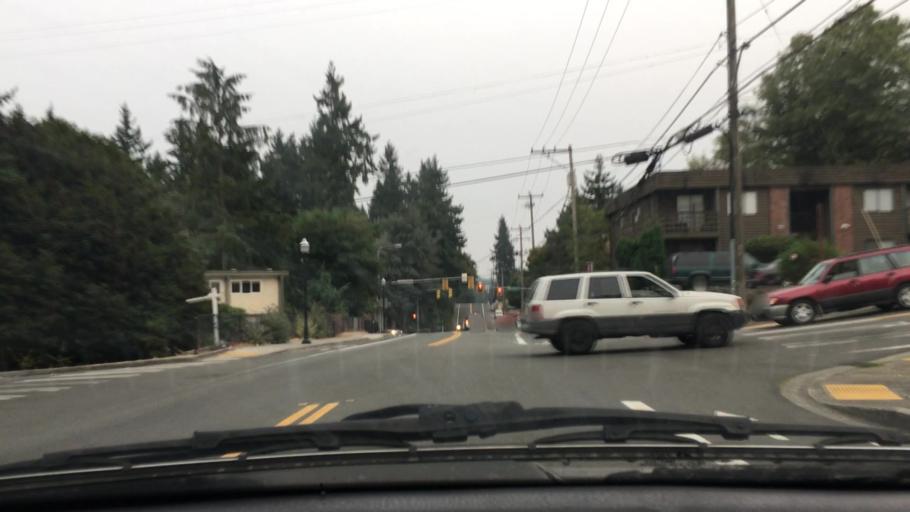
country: US
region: Washington
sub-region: King County
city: Burien
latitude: 47.4644
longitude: -122.3393
